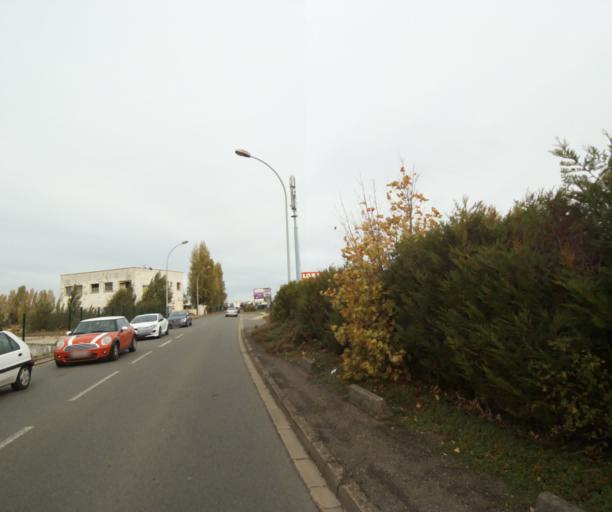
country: FR
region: Centre
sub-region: Departement d'Eure-et-Loir
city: Dreux
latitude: 48.7468
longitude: 1.3645
